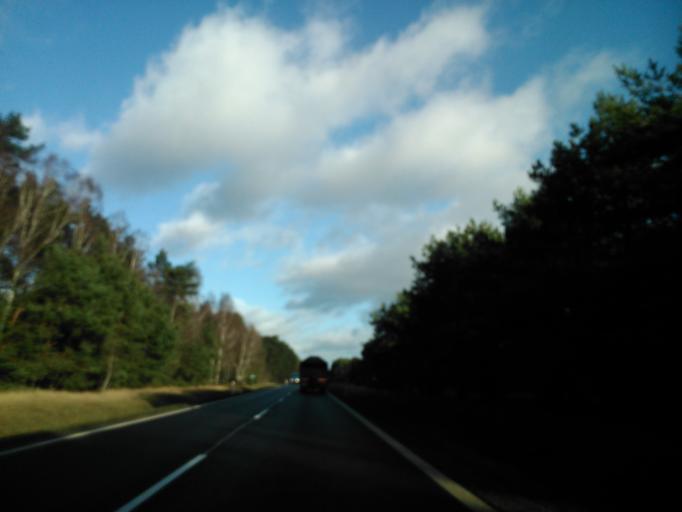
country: PL
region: Kujawsko-Pomorskie
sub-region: Powiat torunski
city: Wielka Nieszawka
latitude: 52.9509
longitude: 18.5277
